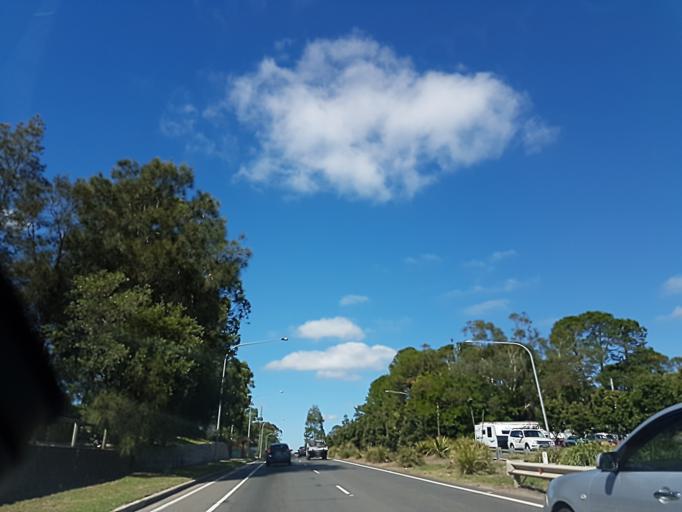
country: AU
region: New South Wales
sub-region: Warringah
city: Davidson
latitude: -33.7175
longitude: 151.2171
